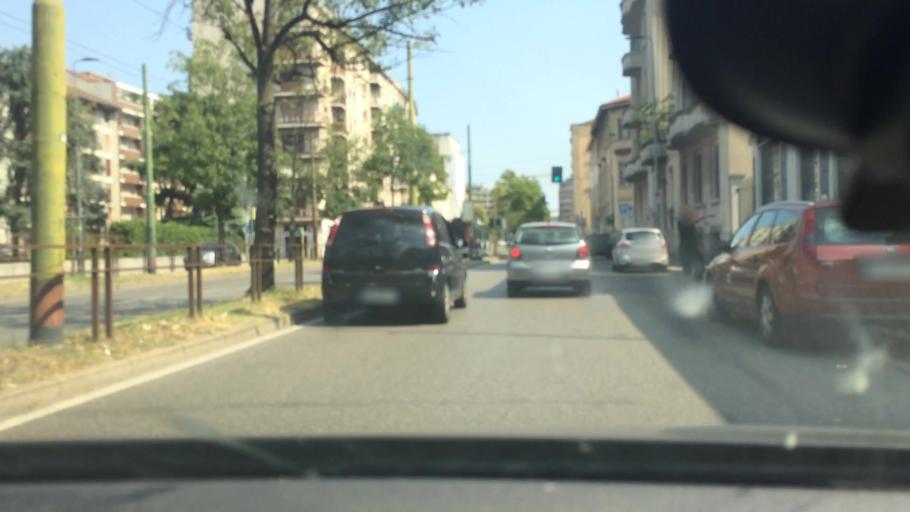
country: IT
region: Lombardy
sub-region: Citta metropolitana di Milano
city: Milano
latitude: 45.4933
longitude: 9.1897
